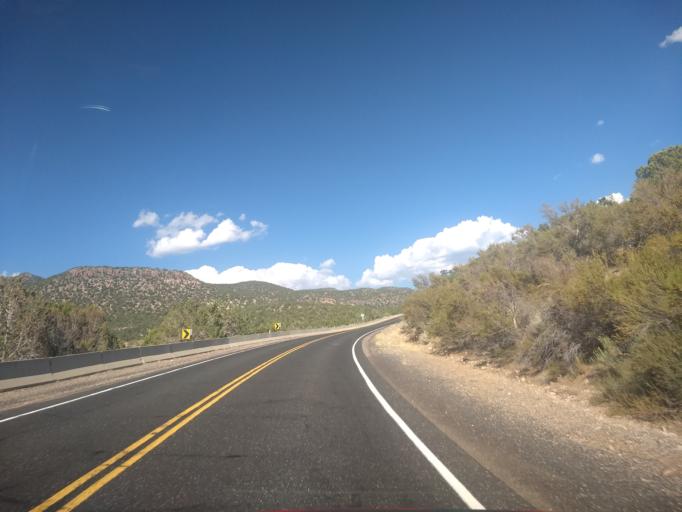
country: US
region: Utah
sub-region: Washington County
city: Enterprise
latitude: 37.4233
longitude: -113.5872
